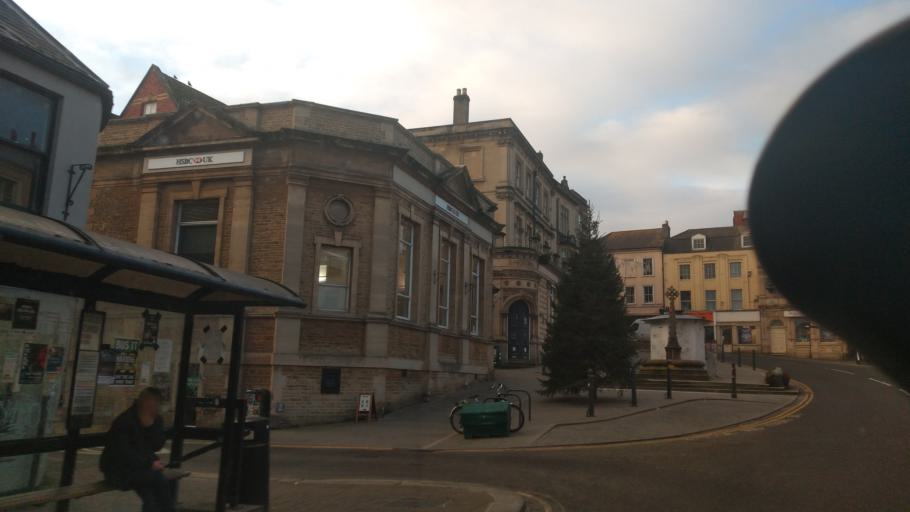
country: GB
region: England
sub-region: Somerset
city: Frome
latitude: 51.2313
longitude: -2.3212
